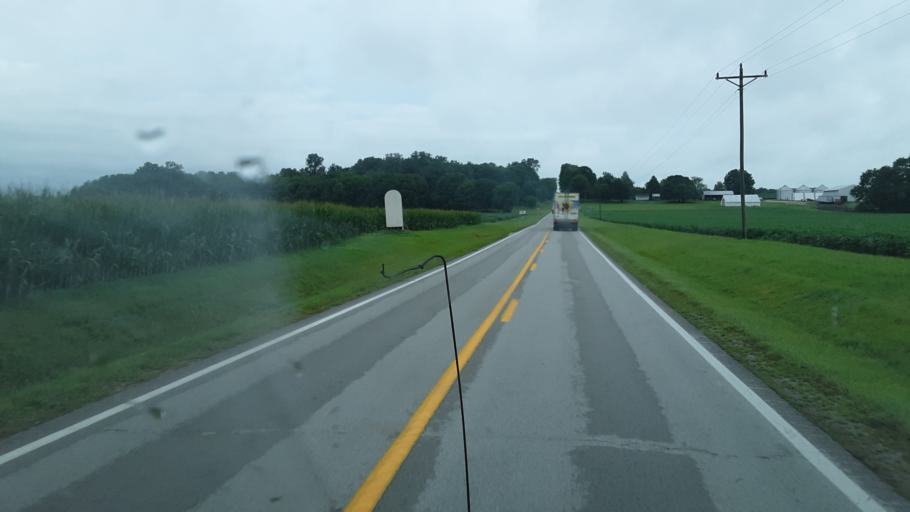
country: US
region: Kentucky
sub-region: Todd County
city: Elkton
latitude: 36.7419
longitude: -87.0582
